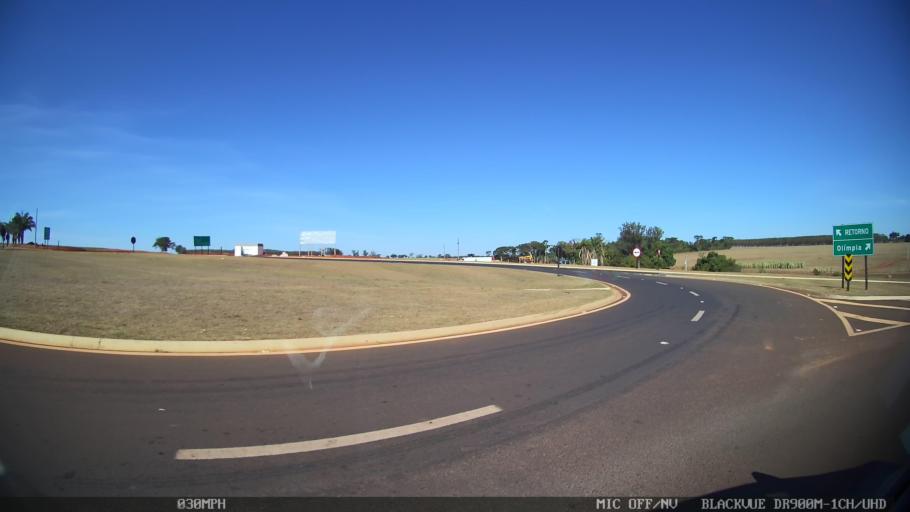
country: BR
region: Sao Paulo
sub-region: Olimpia
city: Olimpia
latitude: -20.7357
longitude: -48.8769
